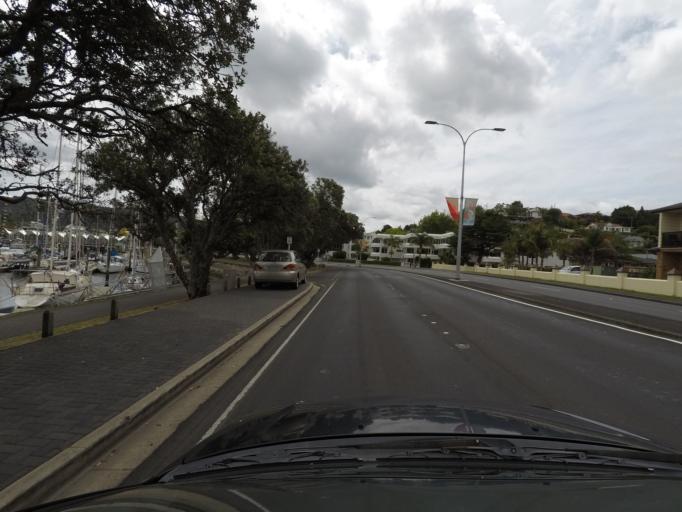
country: NZ
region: Northland
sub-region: Whangarei
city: Whangarei
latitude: -35.7238
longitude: 174.3273
